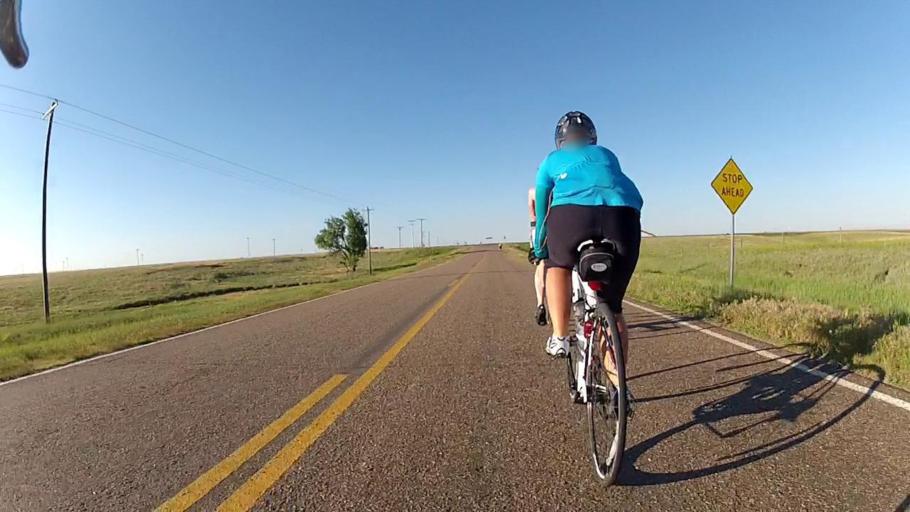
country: US
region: Kansas
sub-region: Ford County
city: Dodge City
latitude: 37.6489
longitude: -99.9070
